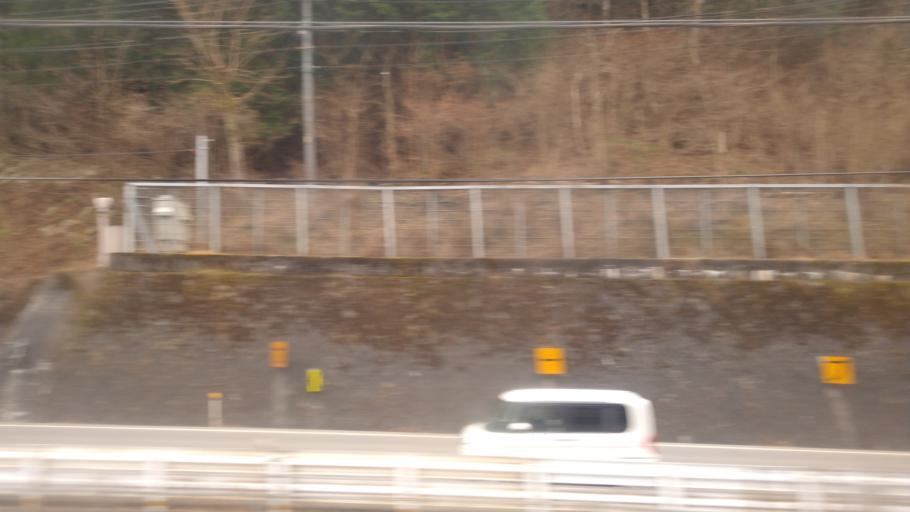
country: JP
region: Nagano
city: Ina
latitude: 35.9263
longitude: 137.7823
